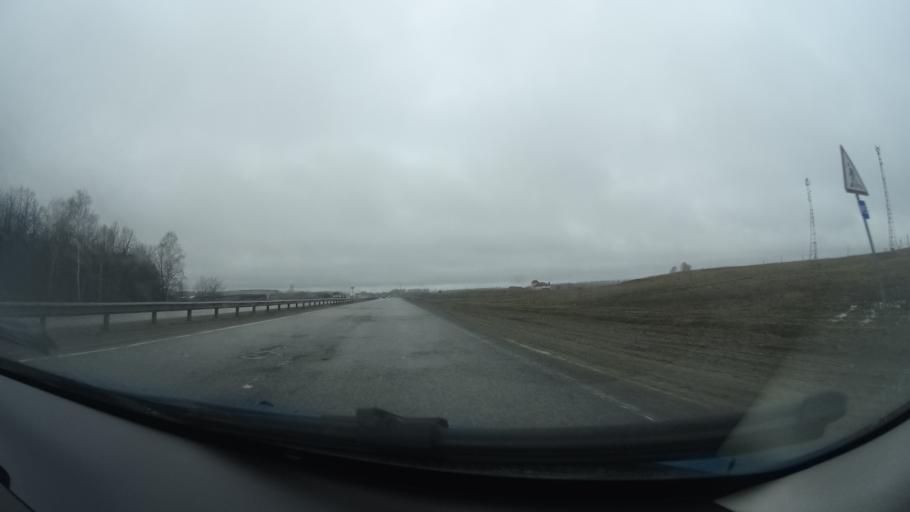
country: RU
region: Bashkortostan
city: Alekseyevka
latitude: 54.7352
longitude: 55.1216
